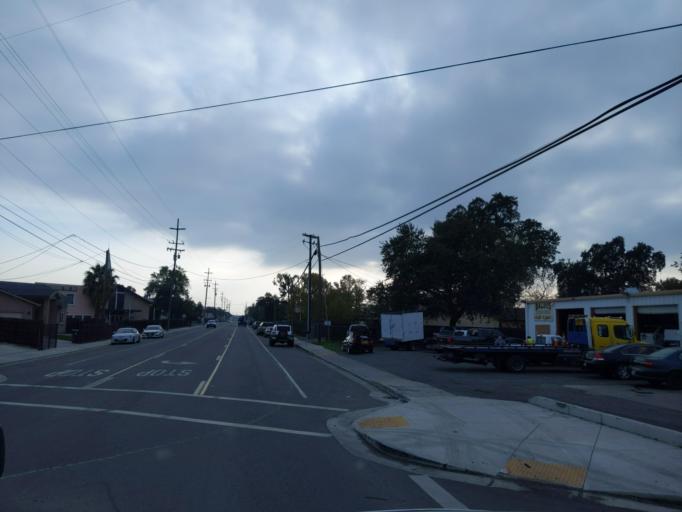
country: US
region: California
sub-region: San Joaquin County
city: August
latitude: 37.9797
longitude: -121.2632
